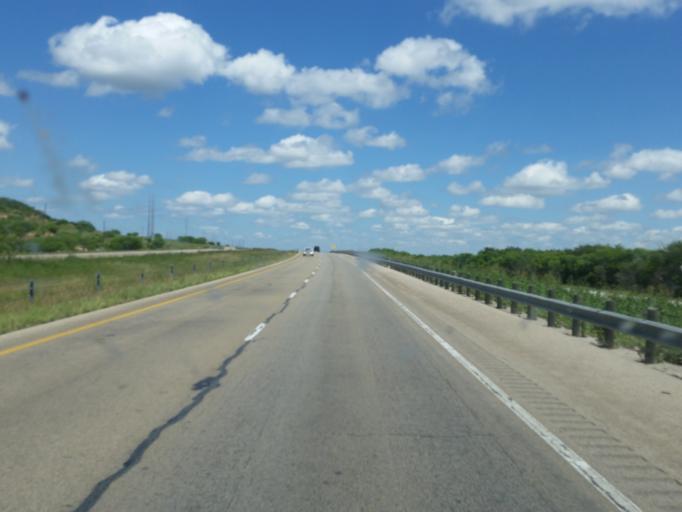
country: US
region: Texas
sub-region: Callahan County
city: Baird
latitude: 32.3918
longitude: -99.3479
